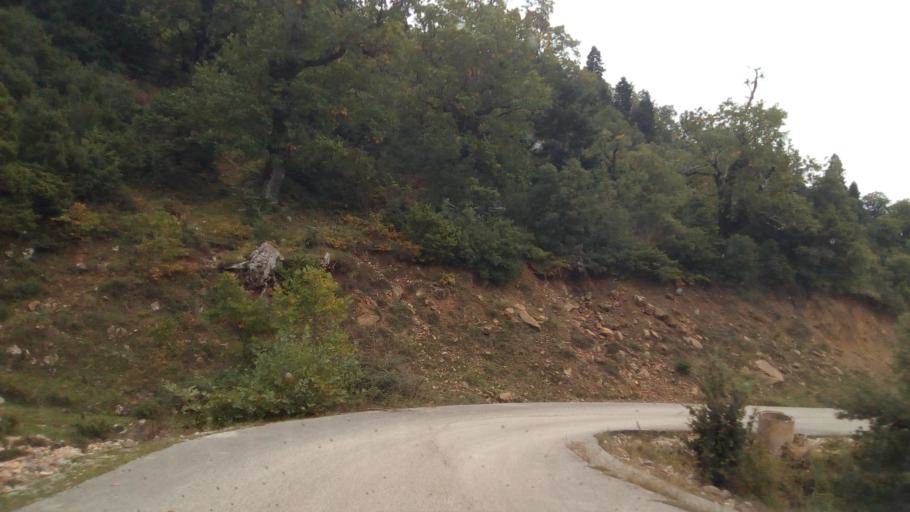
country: GR
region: West Greece
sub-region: Nomos Aitolias kai Akarnanias
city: Thermo
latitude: 38.6117
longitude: 21.8433
